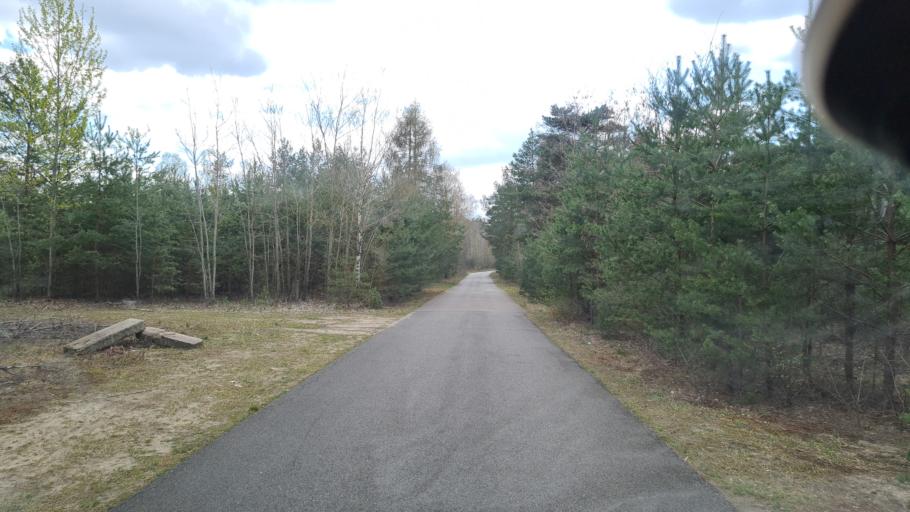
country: DE
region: Brandenburg
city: Senftenberg
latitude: 51.5209
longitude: 14.0959
